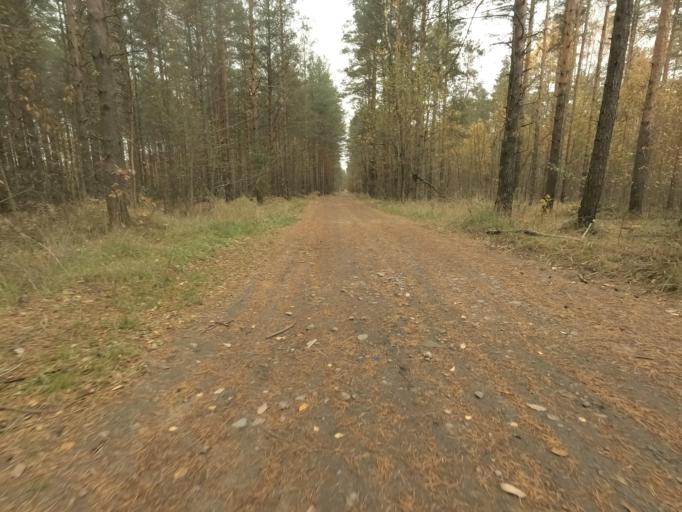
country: RU
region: Leningrad
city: Kirovsk
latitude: 59.8509
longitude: 30.9782
